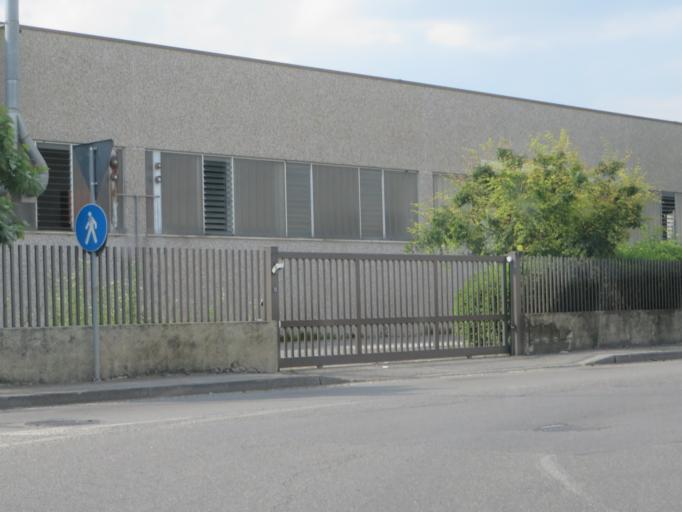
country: IT
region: Lombardy
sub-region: Provincia di Brescia
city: Cologne
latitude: 45.5713
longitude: 9.9451
